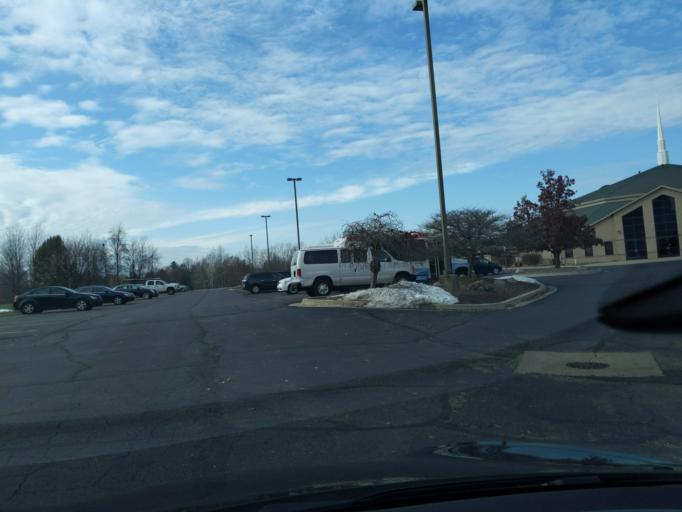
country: US
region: Michigan
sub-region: Ingham County
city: Holt
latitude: 42.6658
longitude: -84.5240
